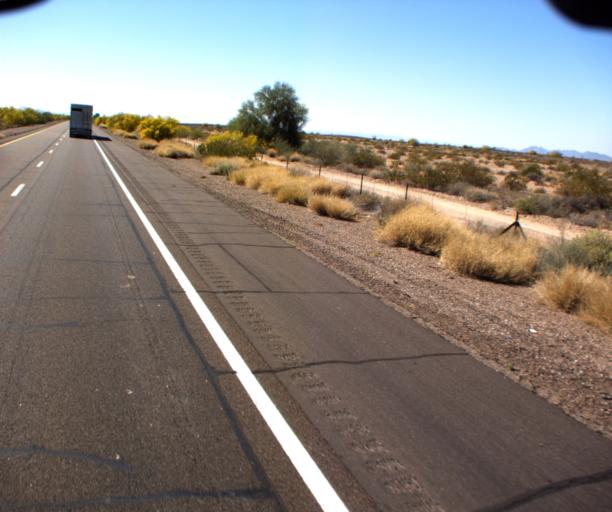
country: US
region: Arizona
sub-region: Maricopa County
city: Gila Bend
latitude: 32.8378
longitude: -113.3417
